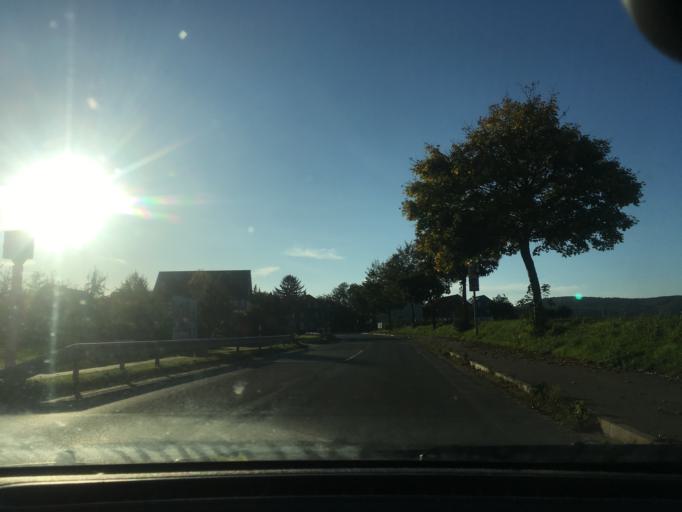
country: DE
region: Lower Saxony
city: Dassel
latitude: 51.8114
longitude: 9.7351
